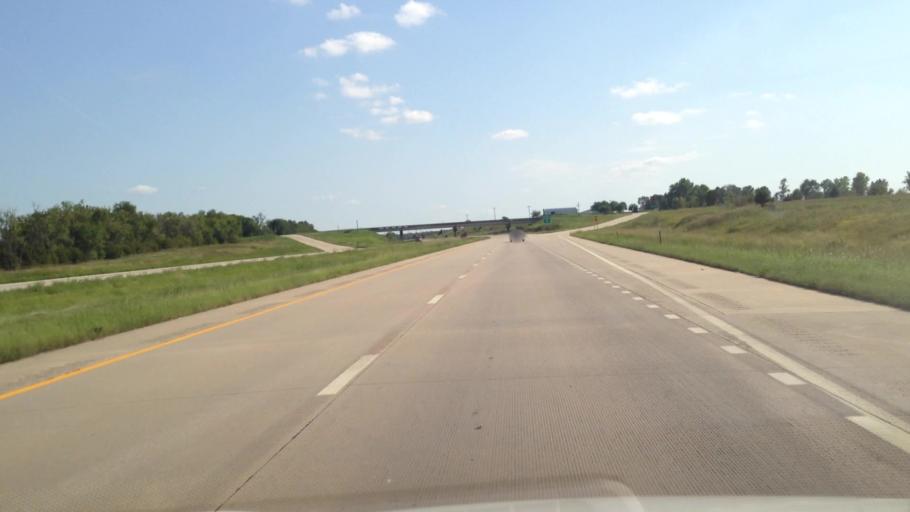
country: US
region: Kansas
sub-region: Bourbon County
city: Fort Scott
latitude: 37.8966
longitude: -94.7049
